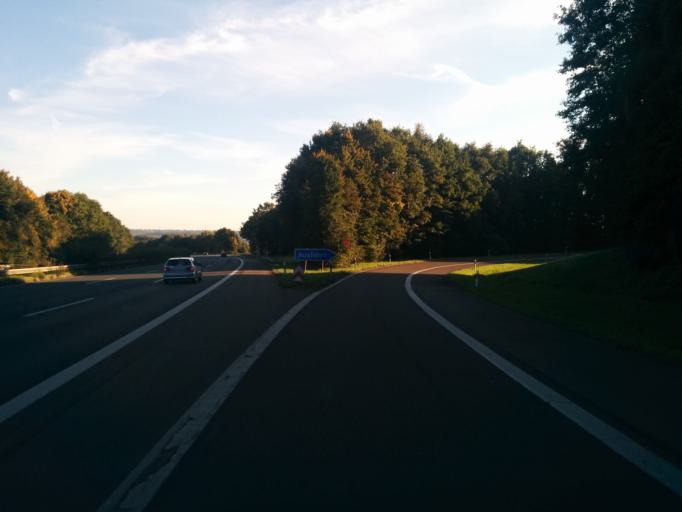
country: DE
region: North Rhine-Westphalia
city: Witten
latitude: 51.4792
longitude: 7.3919
